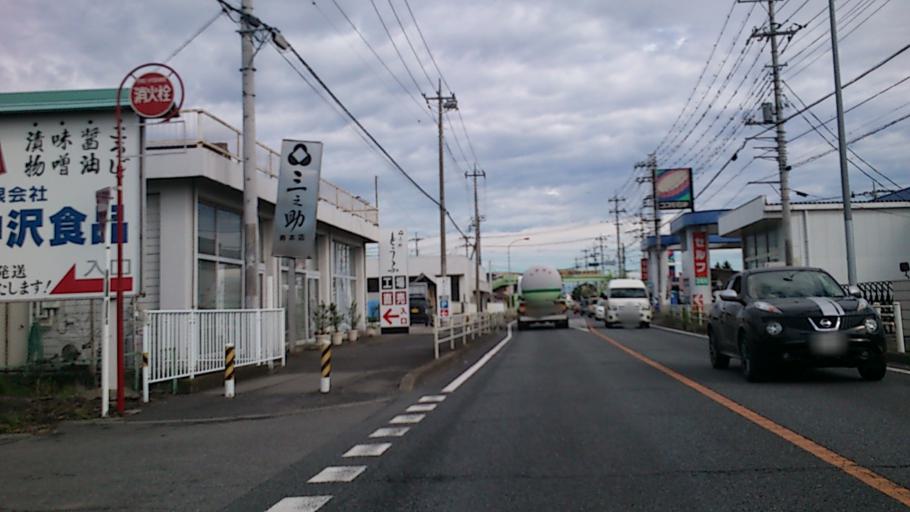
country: JP
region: Saitama
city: Honjo
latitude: 36.2356
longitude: 139.2082
